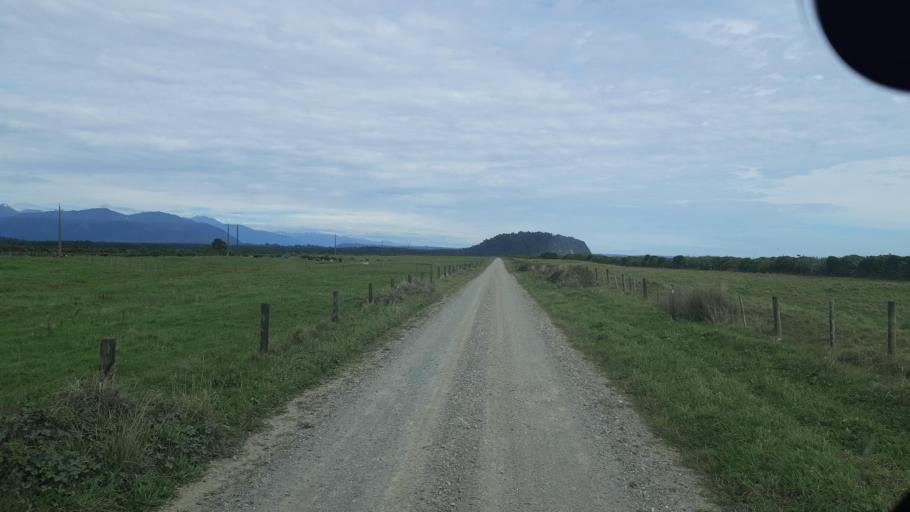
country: NZ
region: West Coast
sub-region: Westland District
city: Hokitika
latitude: -42.9138
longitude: 170.7465
